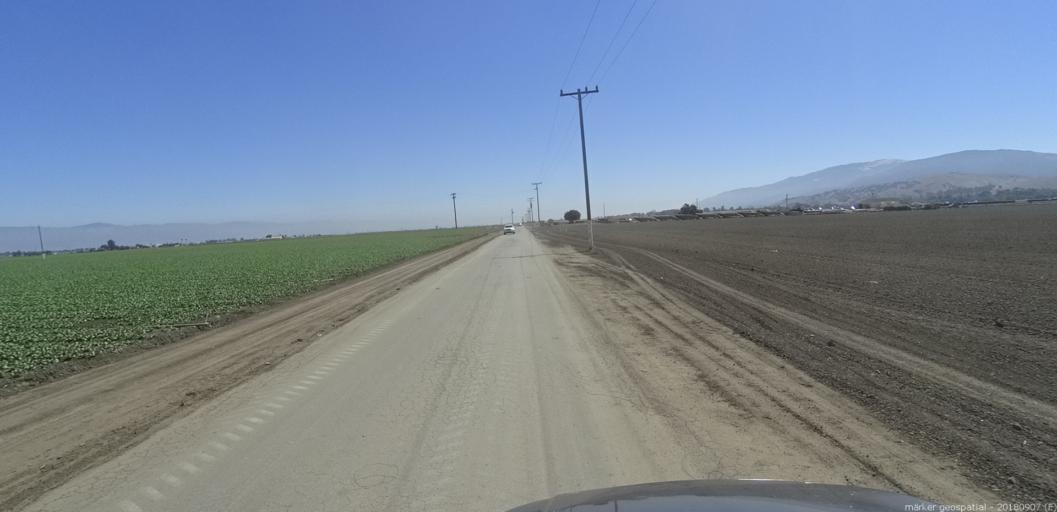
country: US
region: California
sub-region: Monterey County
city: Salinas
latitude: 36.6434
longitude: -121.6828
